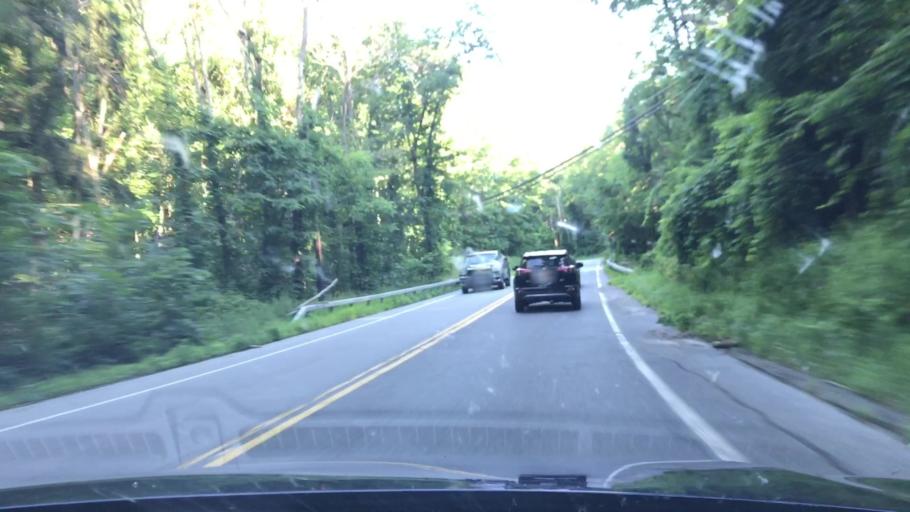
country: US
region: New York
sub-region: Putnam County
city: Mahopac
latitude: 41.3742
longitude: -73.7001
